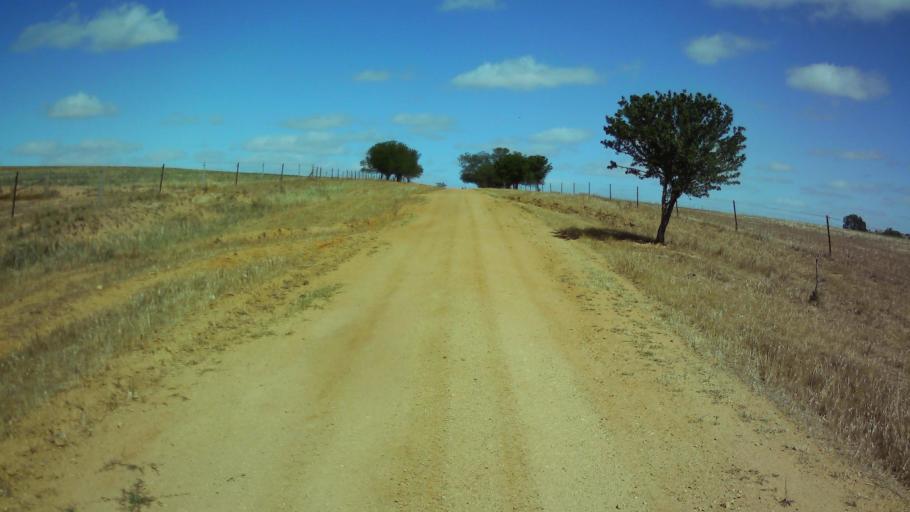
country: AU
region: New South Wales
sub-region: Weddin
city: Grenfell
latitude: -33.9826
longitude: 148.3949
